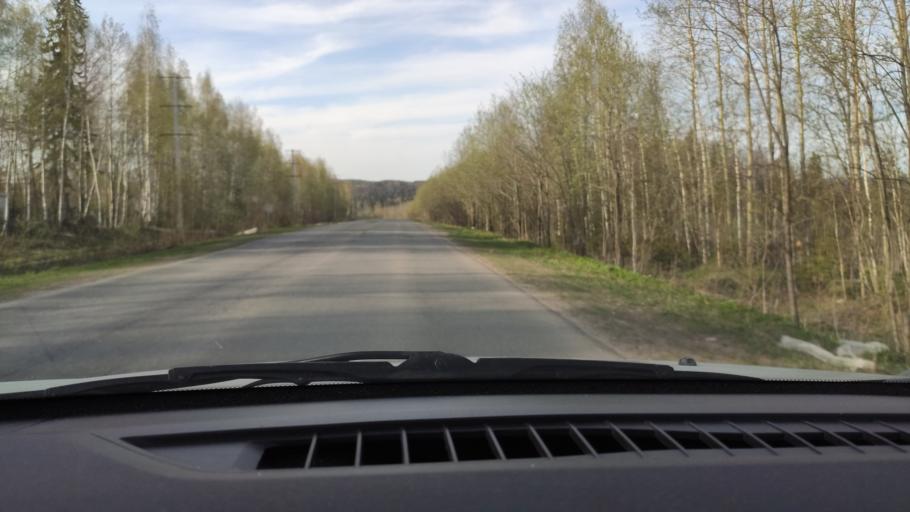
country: RU
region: Perm
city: Novyye Lyady
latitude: 57.9473
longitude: 56.5687
